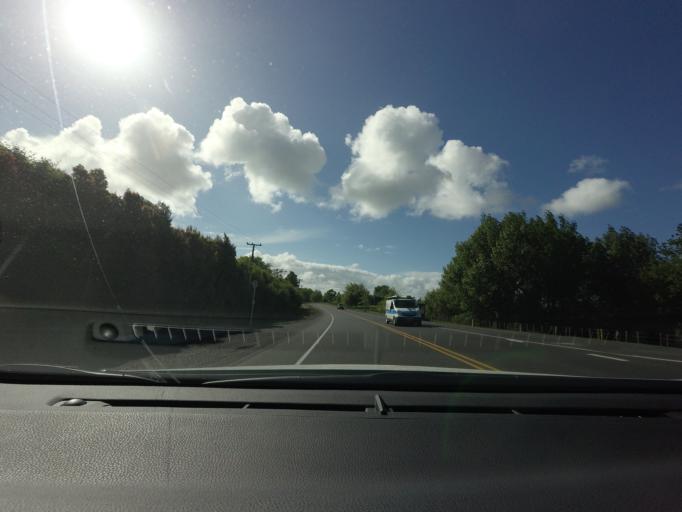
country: NZ
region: Auckland
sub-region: Auckland
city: Rothesay Bay
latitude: -36.6893
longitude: 174.6693
